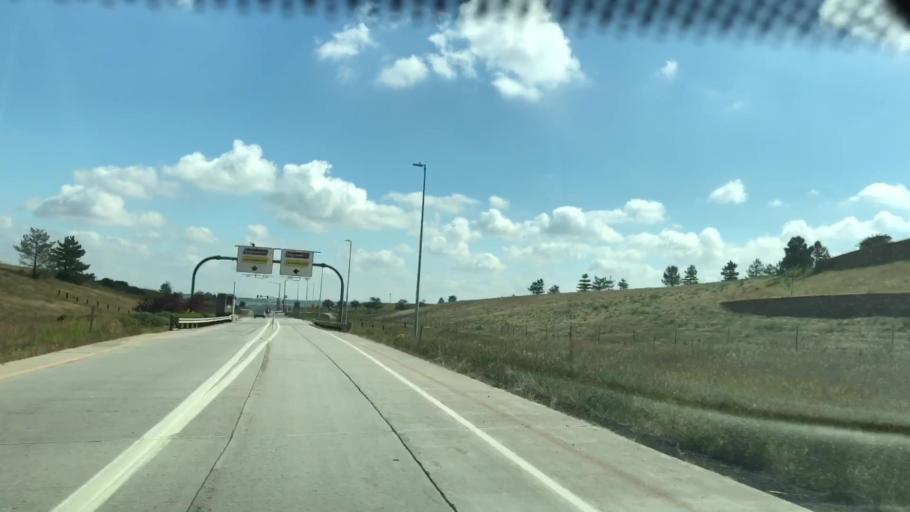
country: US
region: Colorado
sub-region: Douglas County
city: Meridian
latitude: 39.5505
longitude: -104.8435
